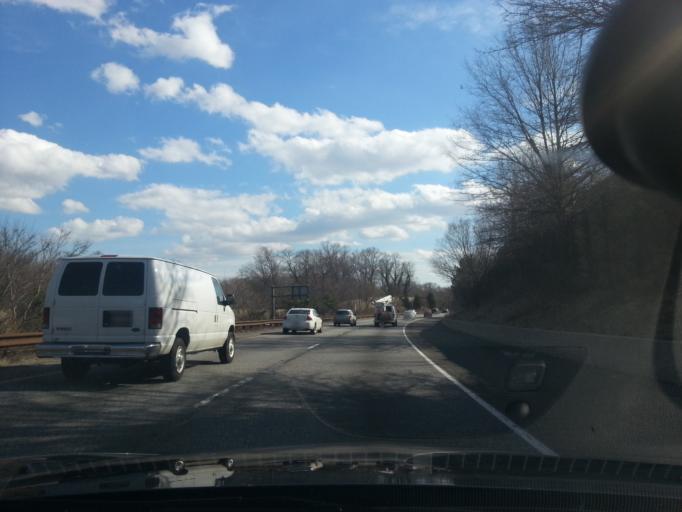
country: US
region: Pennsylvania
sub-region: Delaware County
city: Swarthmore
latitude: 39.8975
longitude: -75.3597
